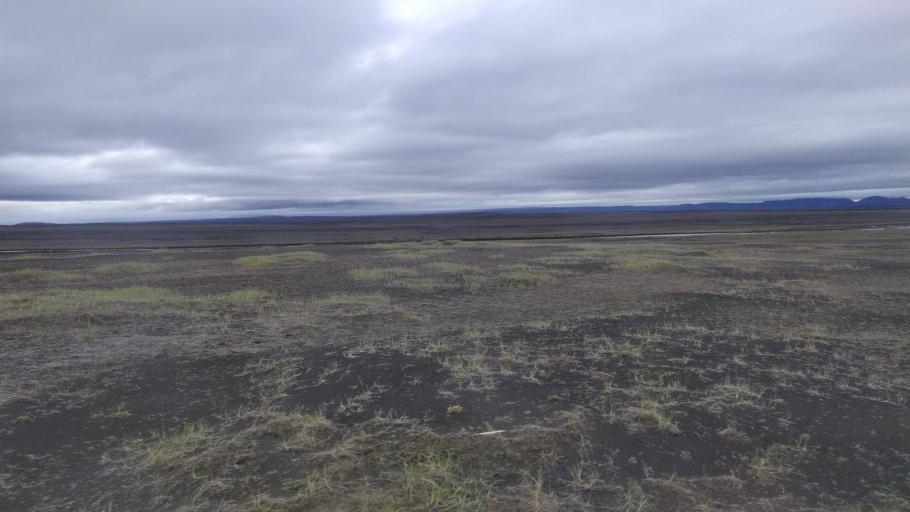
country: IS
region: Northeast
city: Laugar
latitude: 65.6067
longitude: -16.1484
